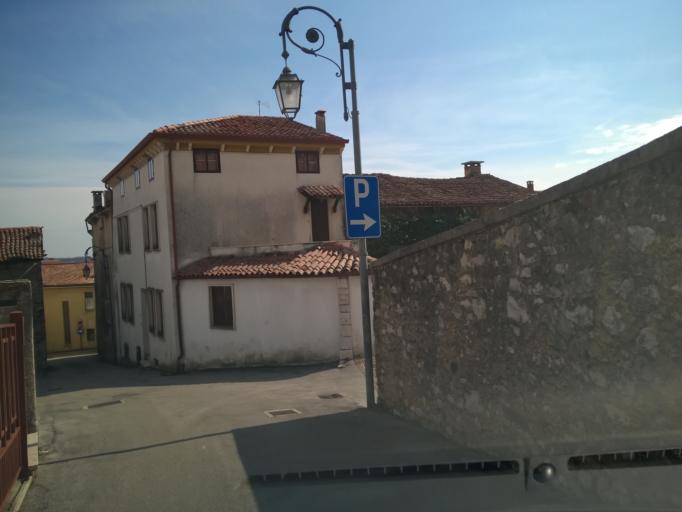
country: IT
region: Veneto
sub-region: Provincia di Vicenza
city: Piovene Rocchette
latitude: 45.7587
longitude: 11.4294
